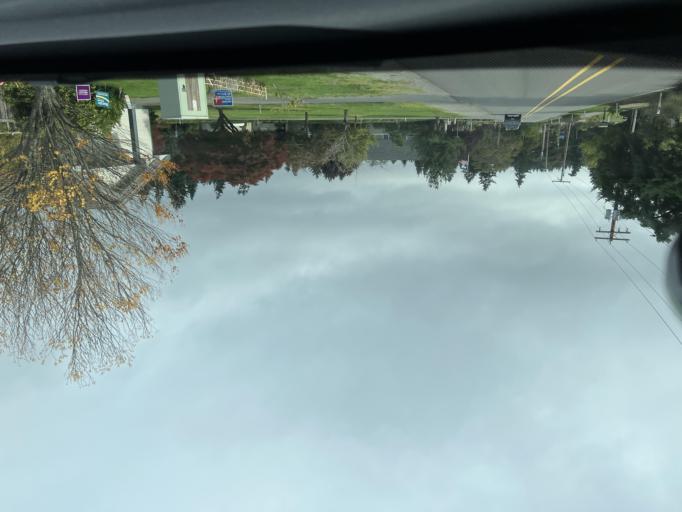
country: US
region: Washington
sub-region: Island County
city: Langley
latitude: 48.0392
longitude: -122.4138
